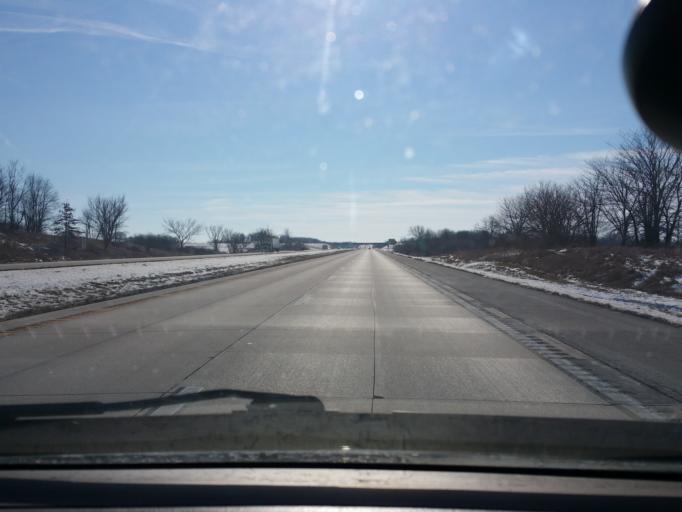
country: US
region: Missouri
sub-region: Daviess County
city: Gallatin
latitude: 40.0044
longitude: -94.0965
